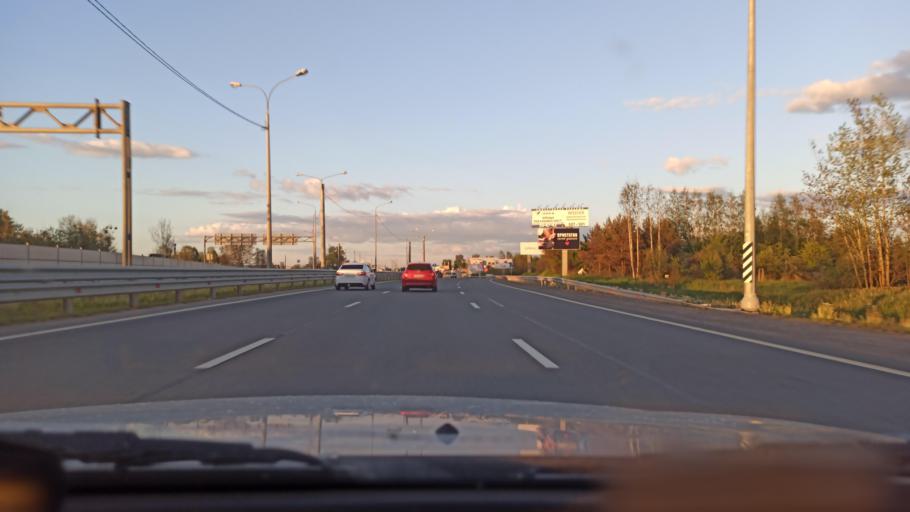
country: RU
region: Vologda
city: Vologda
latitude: 59.2137
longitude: 39.7776
